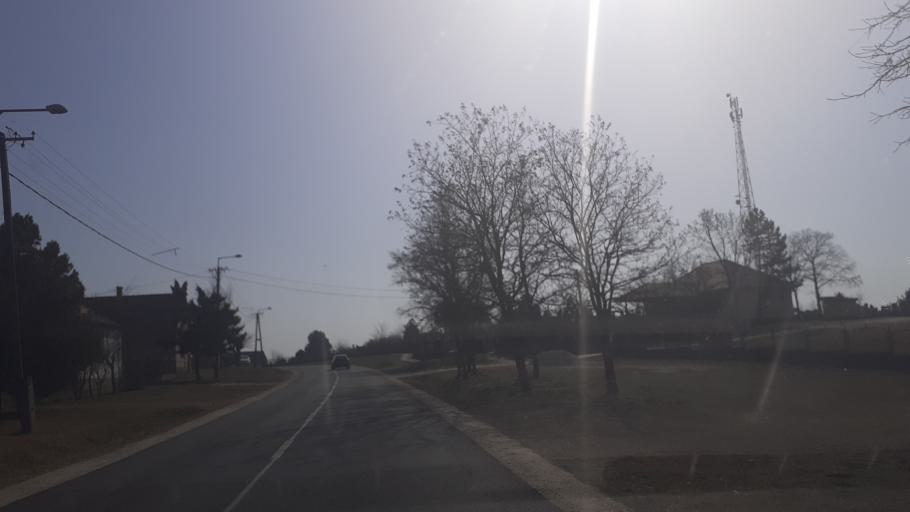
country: HU
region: Pest
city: Orkeny
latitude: 47.0857
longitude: 19.3649
